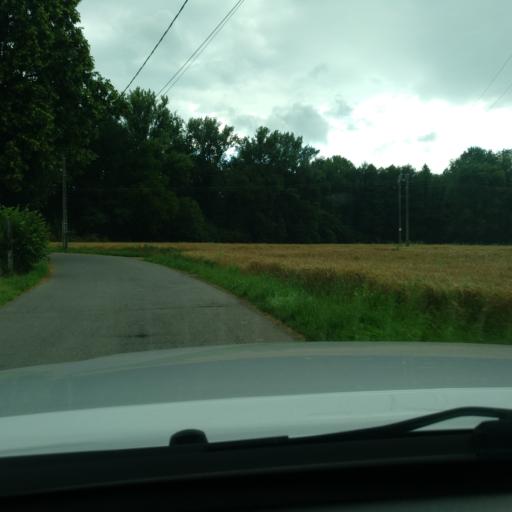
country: FR
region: Rhone-Alpes
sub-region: Departement de la Haute-Savoie
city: Amancy
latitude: 46.0810
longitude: 6.3491
